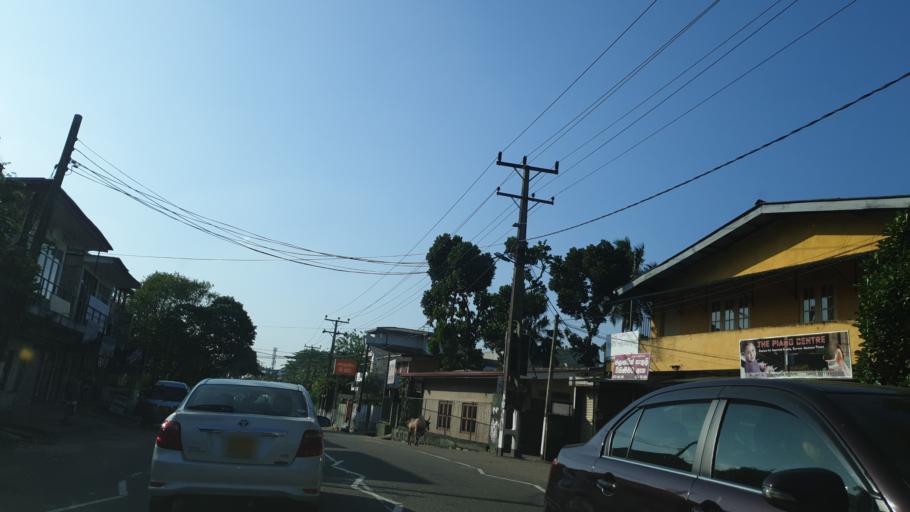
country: LK
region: Western
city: Sri Jayewardenepura Kotte
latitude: 6.8781
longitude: 79.9242
